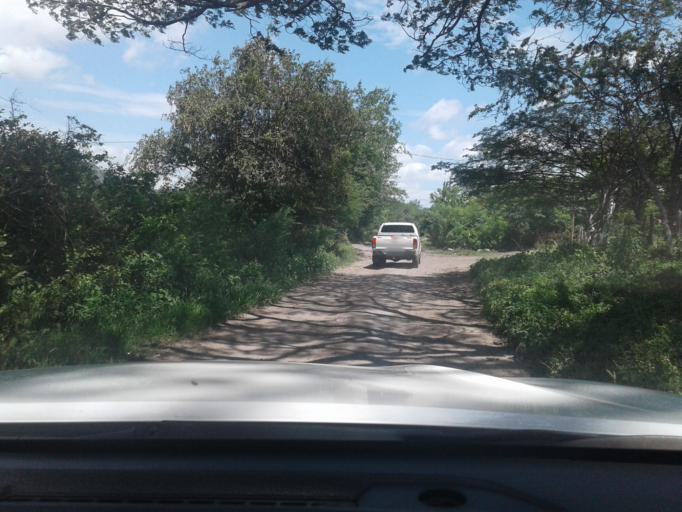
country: NI
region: Matagalpa
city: Terrabona
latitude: 12.5727
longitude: -86.0393
